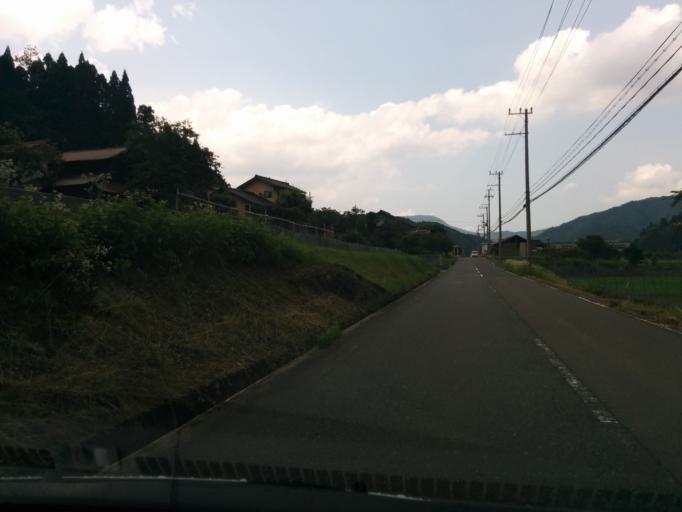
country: JP
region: Kyoto
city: Fukuchiyama
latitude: 35.4064
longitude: 135.1507
